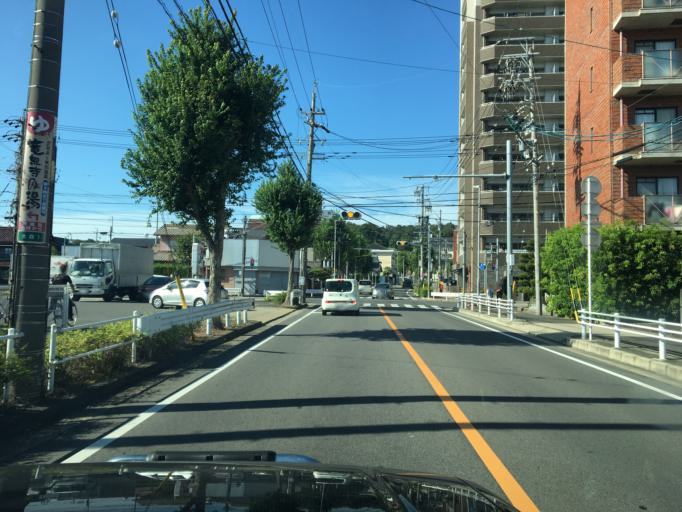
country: JP
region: Aichi
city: Kasugai
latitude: 35.2052
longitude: 136.9964
